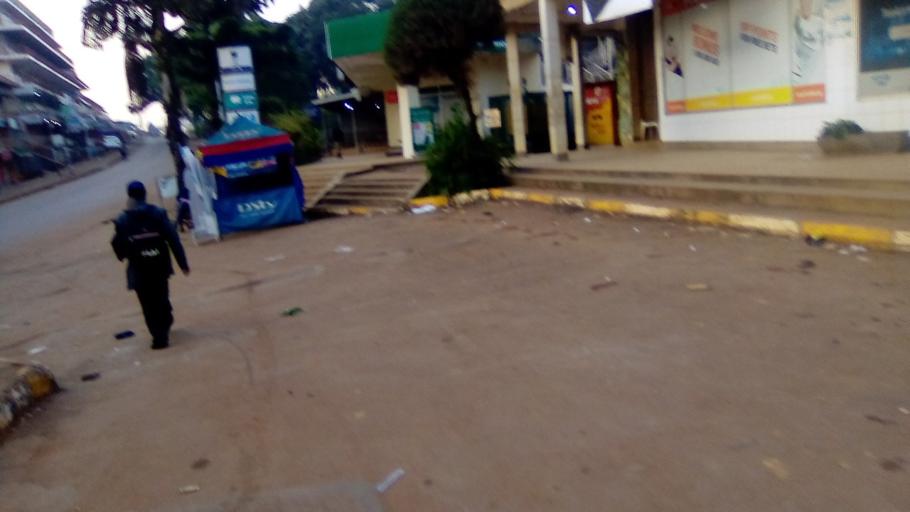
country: UG
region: Central Region
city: Masaka
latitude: -0.3406
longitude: 31.7374
